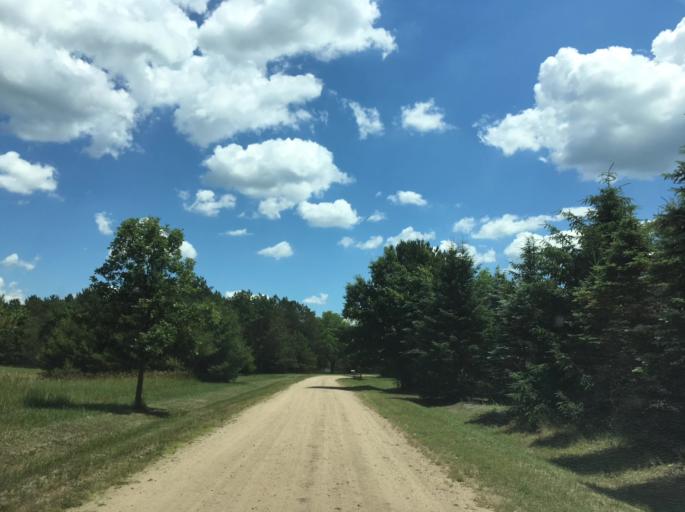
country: US
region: Michigan
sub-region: Osceola County
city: Evart
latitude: 43.8608
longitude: -85.3775
